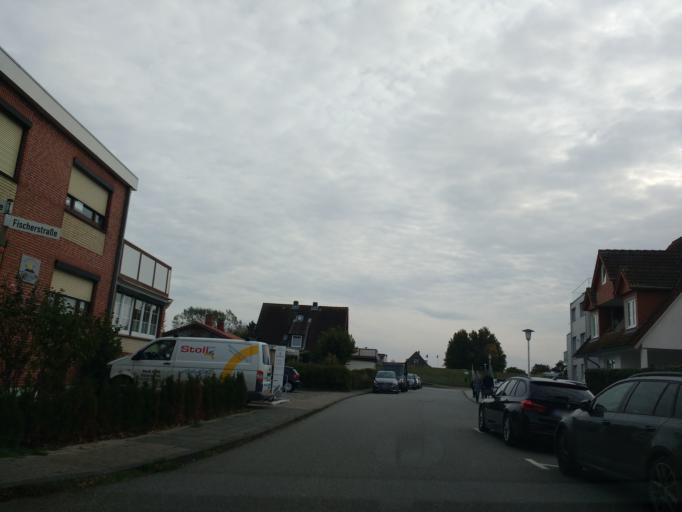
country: DE
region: Schleswig-Holstein
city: Gromitz
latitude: 54.1471
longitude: 10.9643
